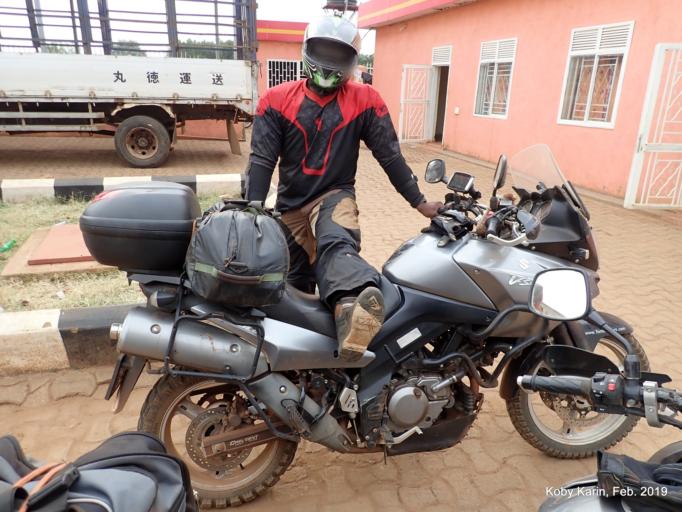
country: UG
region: Western Region
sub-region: Kasese District
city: Kasese
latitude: 0.3528
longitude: 30.2001
